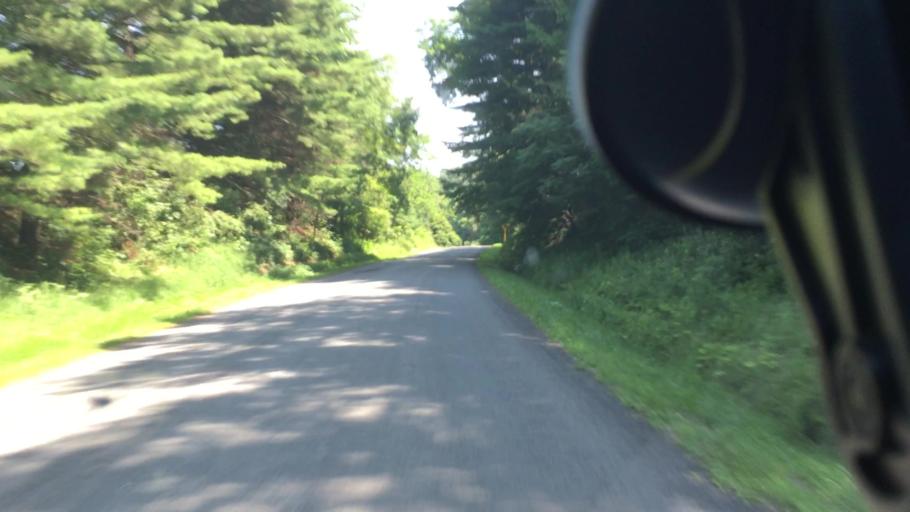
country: US
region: Ohio
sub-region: Columbiana County
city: Lisbon
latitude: 40.7677
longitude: -80.7917
